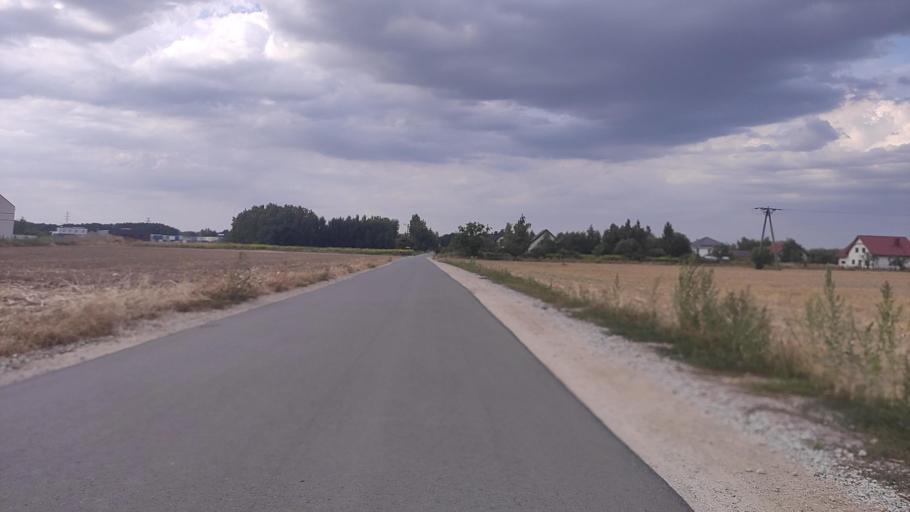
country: PL
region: Greater Poland Voivodeship
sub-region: Powiat poznanski
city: Swarzedz
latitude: 52.4183
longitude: 17.1012
